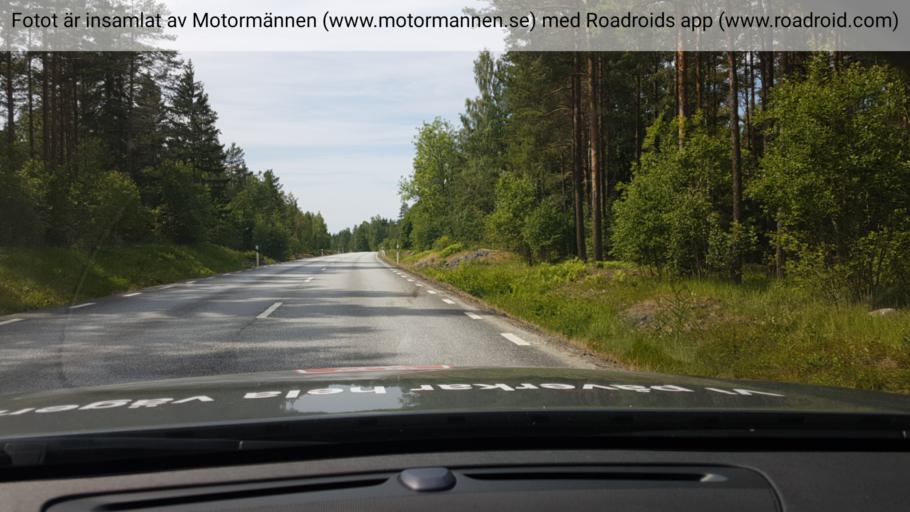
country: SE
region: Uppsala
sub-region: Osthammars Kommun
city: Anneberg
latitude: 60.1750
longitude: 18.4204
